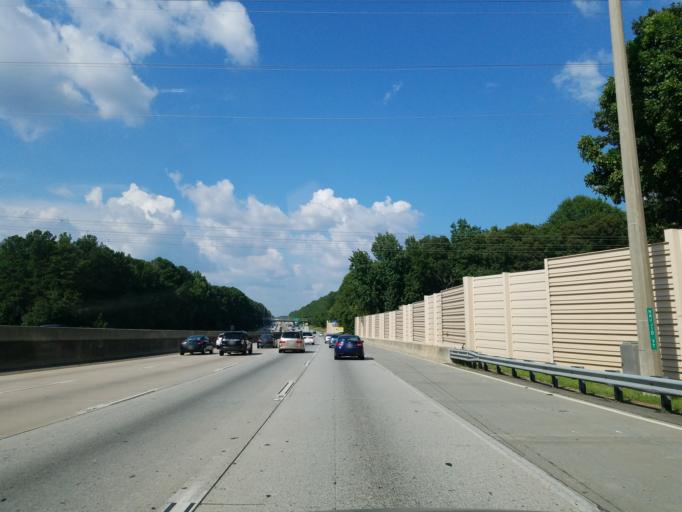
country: US
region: Georgia
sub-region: DeKalb County
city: Dunwoody
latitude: 33.9651
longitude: -84.3504
